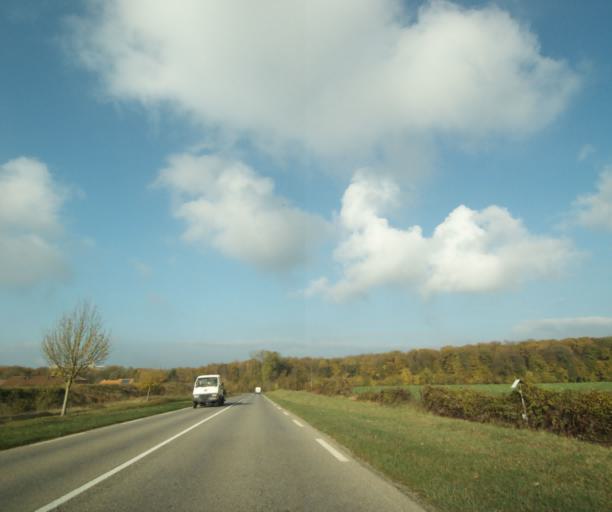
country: FR
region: Lorraine
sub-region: Departement de Meurthe-et-Moselle
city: Briey
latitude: 49.2589
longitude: 5.9414
